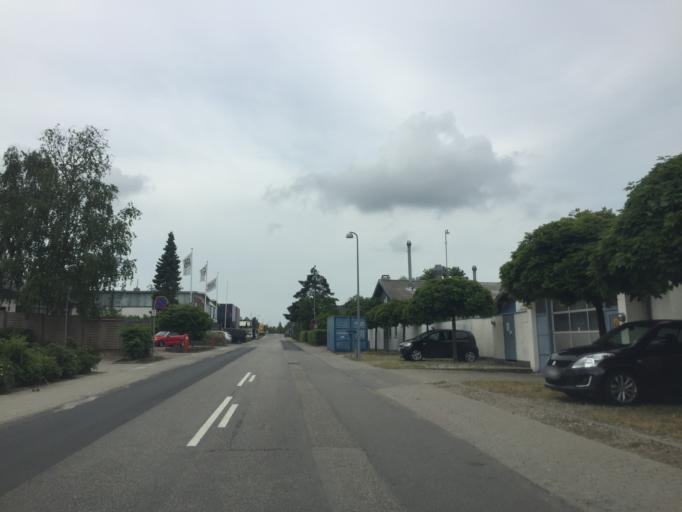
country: DK
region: Capital Region
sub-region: Fureso Kommune
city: Farum
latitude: 55.8175
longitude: 12.3701
